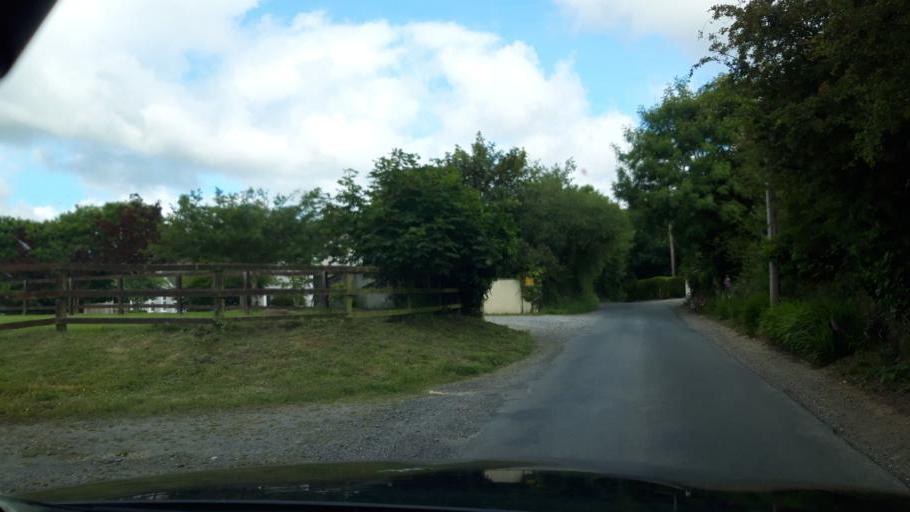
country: IE
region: Leinster
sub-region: Loch Garman
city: Loch Garman
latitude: 52.2828
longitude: -6.4977
